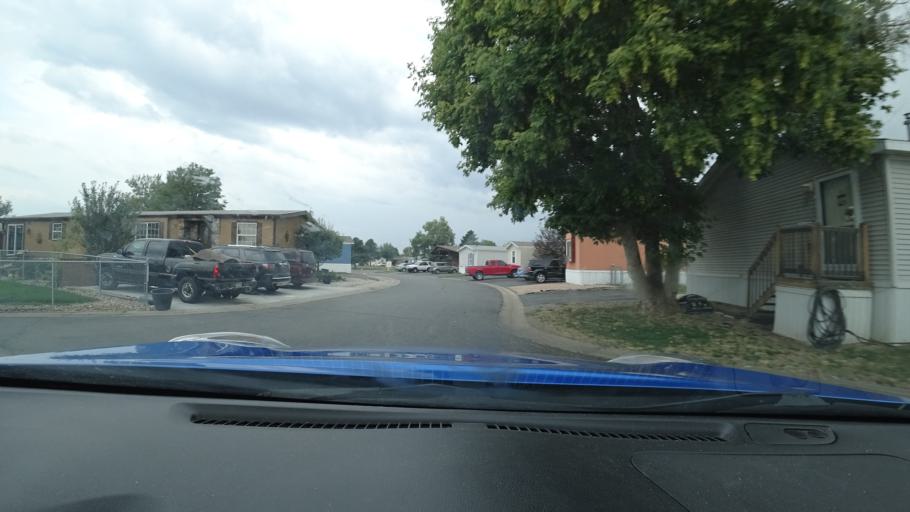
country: US
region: Colorado
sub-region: Adams County
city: Aurora
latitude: 39.7424
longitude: -104.7841
